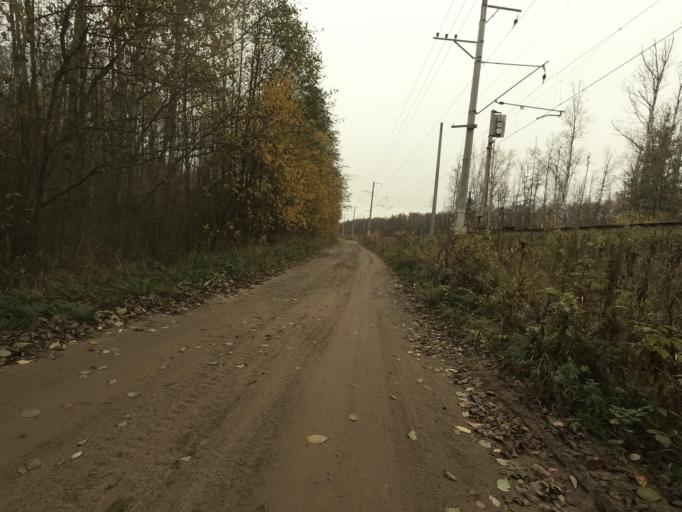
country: RU
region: Leningrad
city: Pavlovo
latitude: 59.7851
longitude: 30.8924
